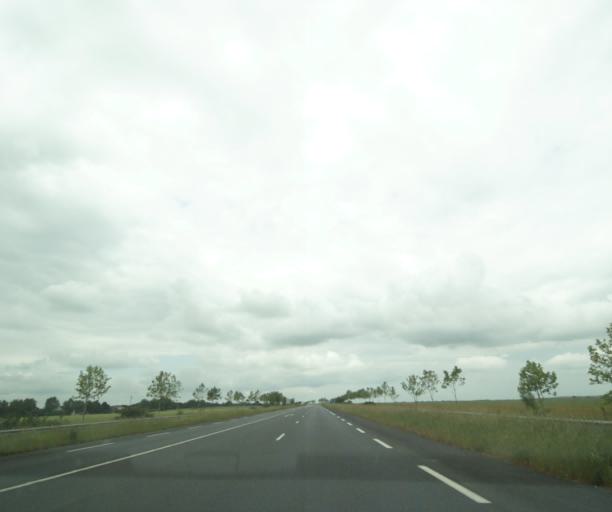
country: FR
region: Poitou-Charentes
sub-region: Departement des Deux-Sevres
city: Saint-Varent
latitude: 46.8974
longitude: -0.1923
